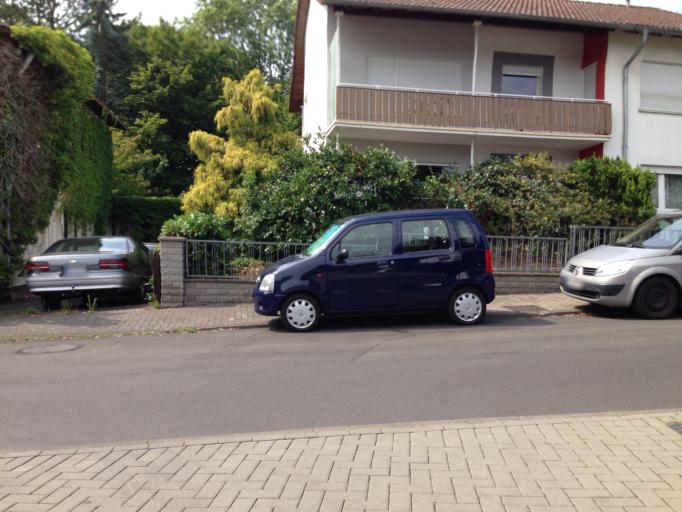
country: DE
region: Hesse
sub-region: Regierungsbezirk Giessen
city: Giessen
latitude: 50.5797
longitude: 8.7032
